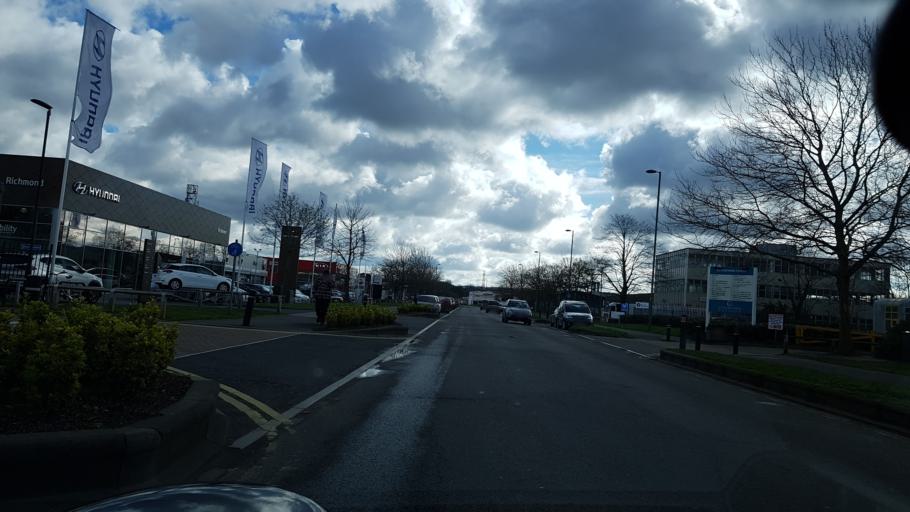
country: GB
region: England
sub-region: Surrey
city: Guildford
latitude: 51.2609
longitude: -0.5663
